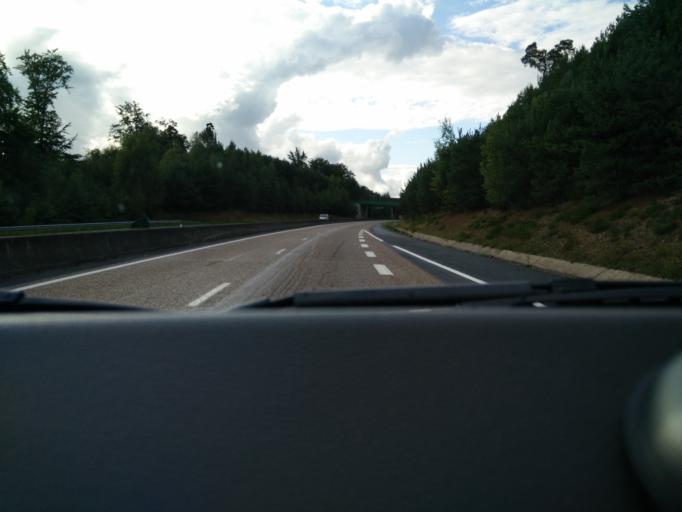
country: FR
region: Lorraine
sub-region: Departement de Meurthe-et-Moselle
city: Baccarat
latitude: 48.4394
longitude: 6.7648
